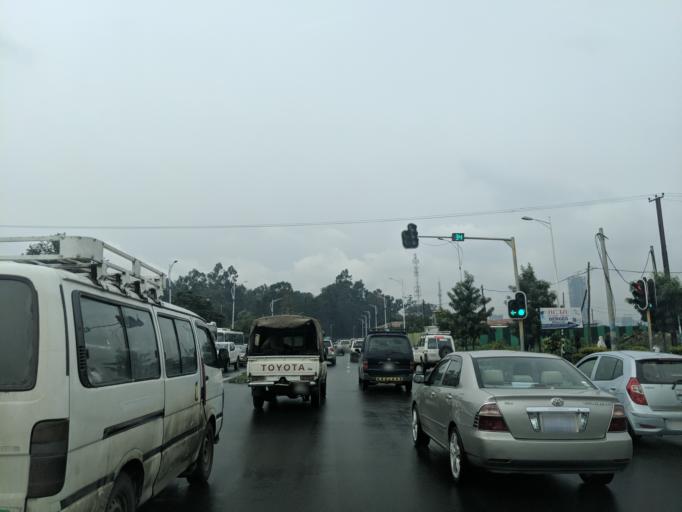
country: ET
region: Adis Abeba
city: Addis Ababa
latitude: 9.0298
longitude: 38.7635
